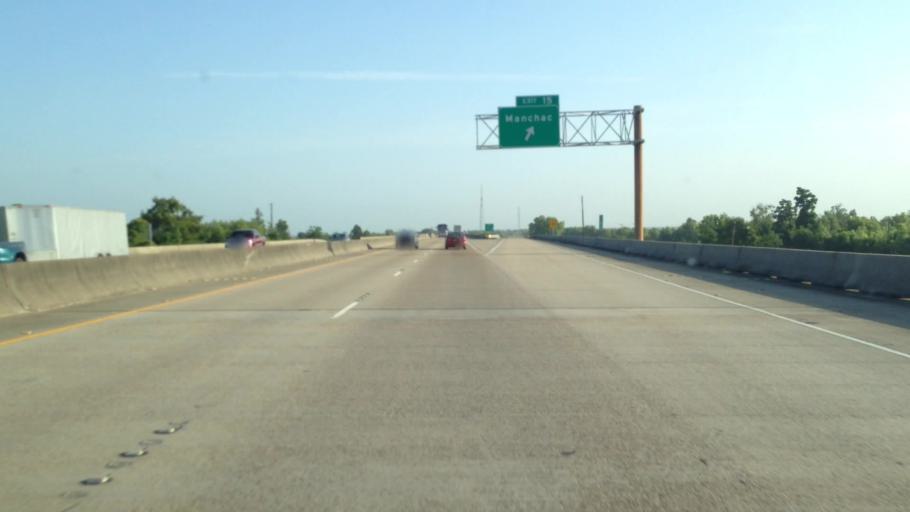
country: US
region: Louisiana
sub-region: Tangipahoa Parish
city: Ponchatoula
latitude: 30.2921
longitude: -90.4032
